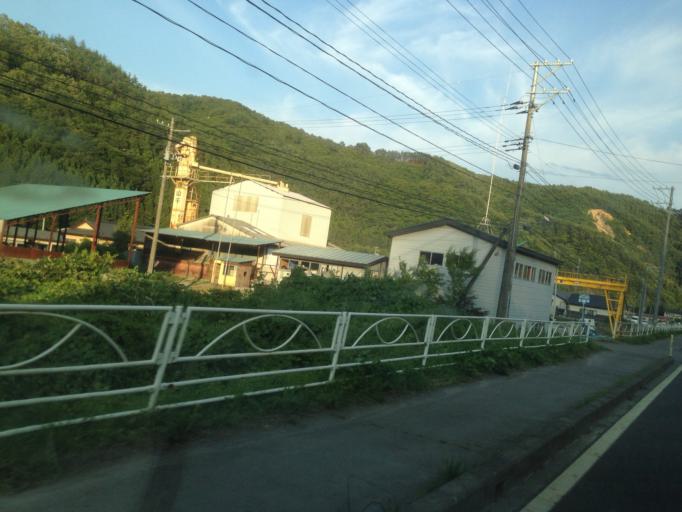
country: JP
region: Iwate
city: Otsuchi
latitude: 39.3818
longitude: 141.8840
